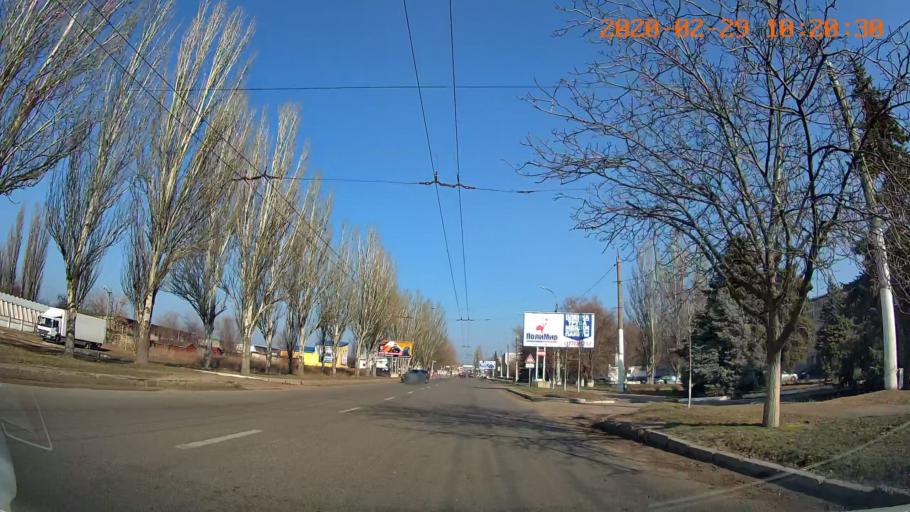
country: MD
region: Telenesti
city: Tiraspolul Nou
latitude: 46.8608
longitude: 29.6105
